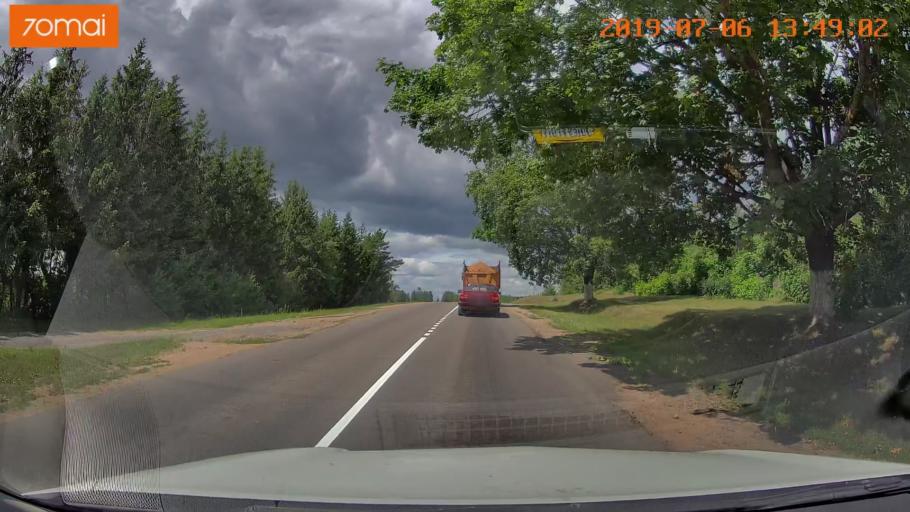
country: BY
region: Minsk
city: Ivyanyets
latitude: 53.6925
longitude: 26.8537
